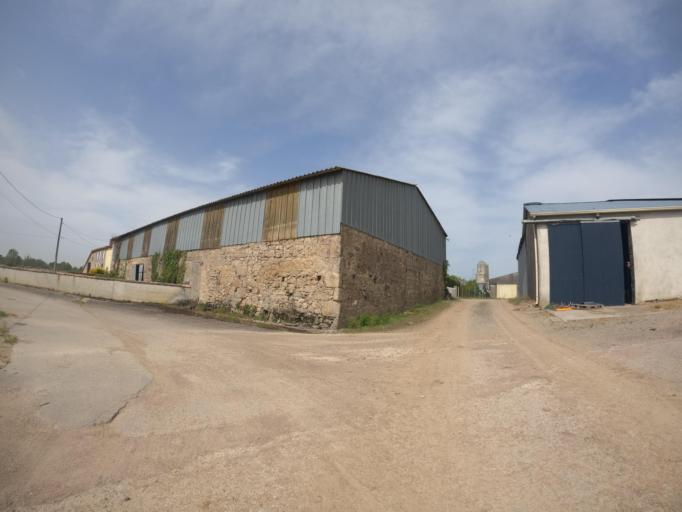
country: FR
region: Poitou-Charentes
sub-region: Departement des Deux-Sevres
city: La Chapelle-Saint-Laurent
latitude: 46.7109
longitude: -0.5100
